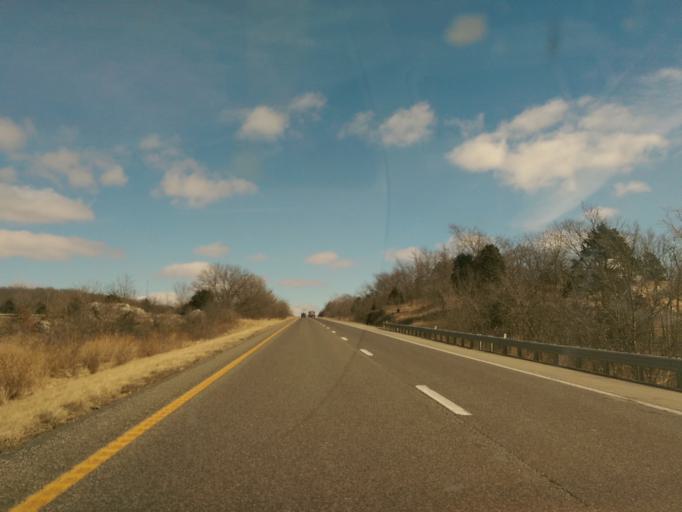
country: US
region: Missouri
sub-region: Montgomery County
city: Montgomery City
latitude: 38.9007
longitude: -91.5777
